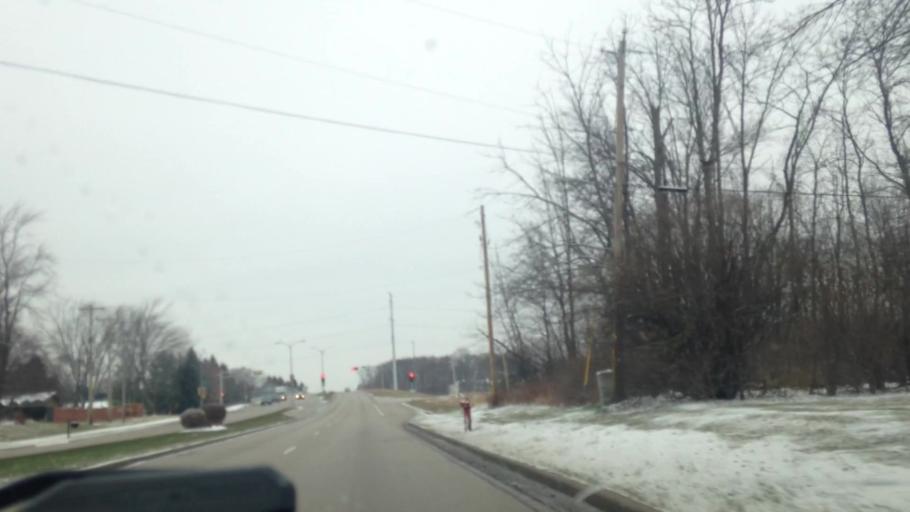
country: US
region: Wisconsin
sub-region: Waukesha County
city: Butler
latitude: 43.1226
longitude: -88.1051
